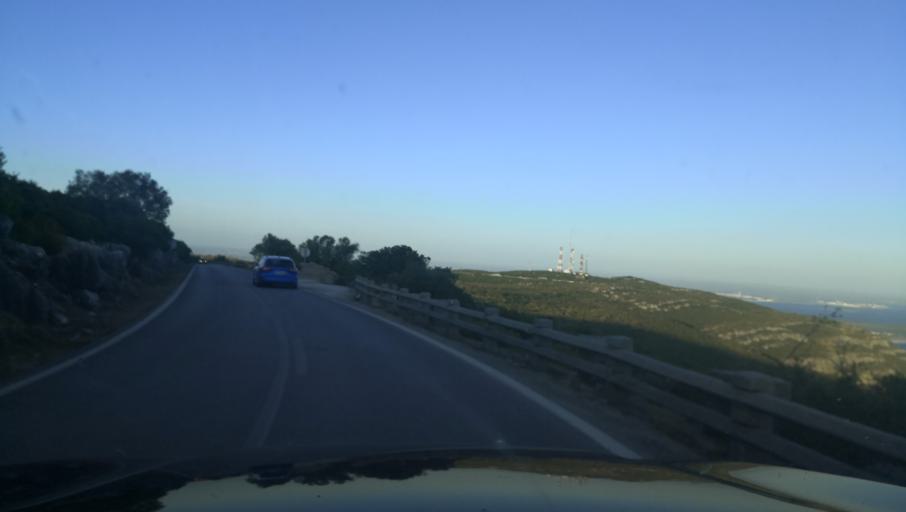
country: PT
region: Setubal
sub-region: Palmela
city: Quinta do Anjo
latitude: 38.4908
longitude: -8.9718
